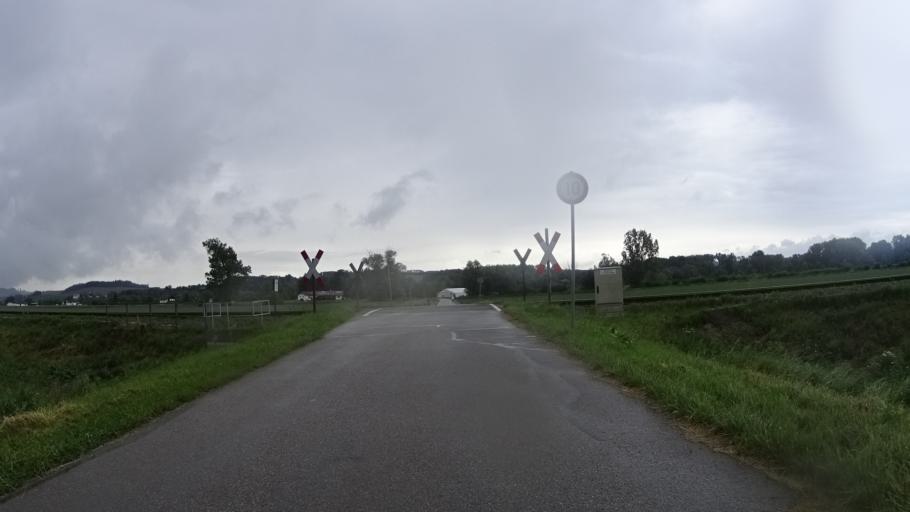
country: DE
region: Bavaria
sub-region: Lower Bavaria
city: Pocking
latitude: 48.4069
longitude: 13.2884
